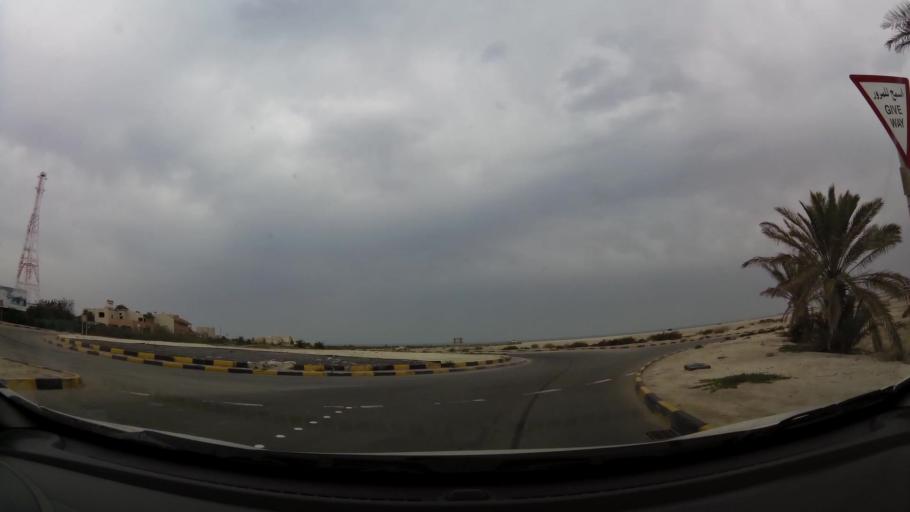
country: BH
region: Central Governorate
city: Dar Kulayb
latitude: 25.9957
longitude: 50.4686
